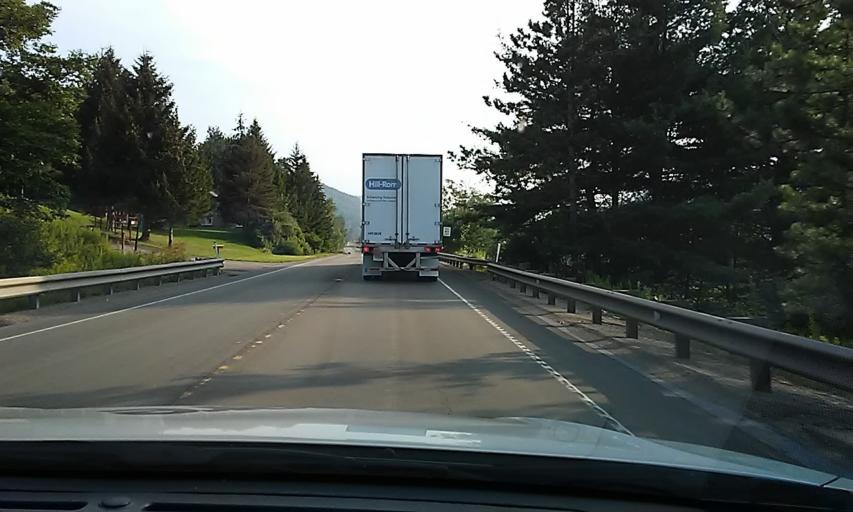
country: US
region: Pennsylvania
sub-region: McKean County
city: Smethport
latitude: 41.7401
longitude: -78.5340
